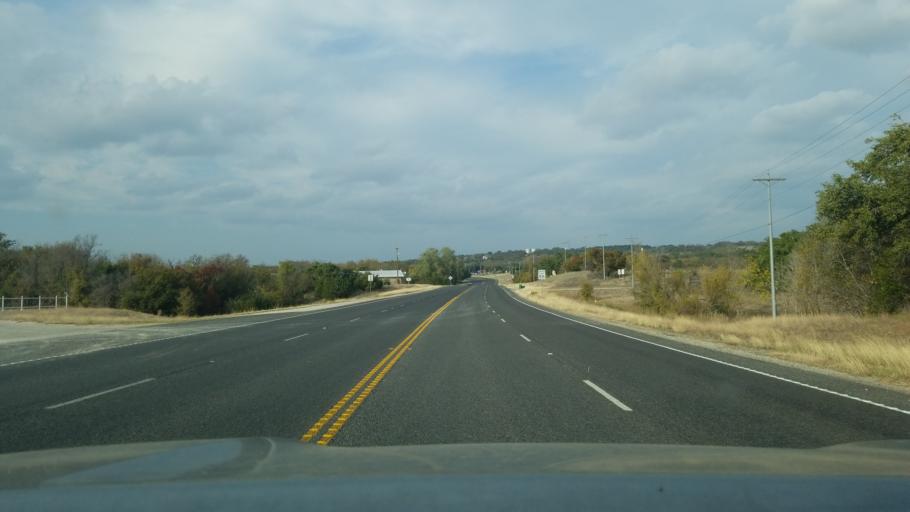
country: US
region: Texas
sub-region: Mills County
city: Goldthwaite
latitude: 31.4400
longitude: -98.5682
